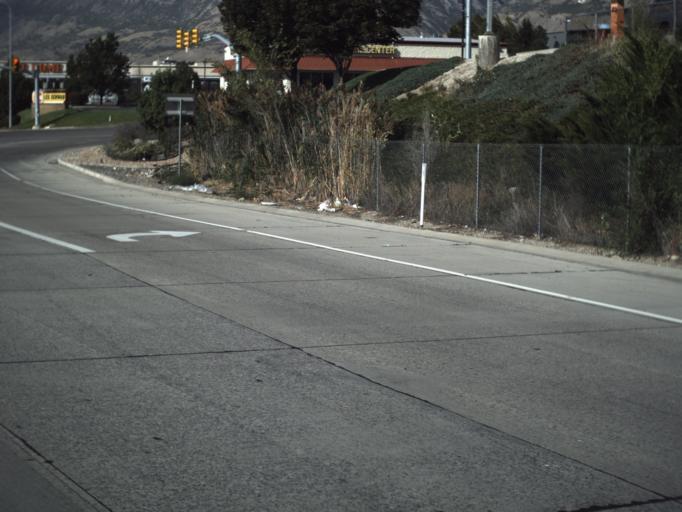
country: US
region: Utah
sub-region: Utah County
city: Lindon
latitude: 40.3255
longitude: -111.7293
